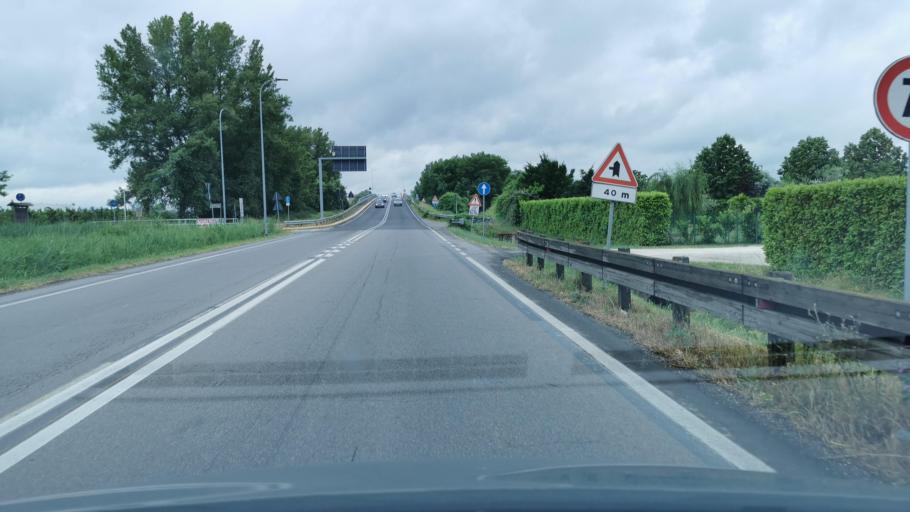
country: IT
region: Emilia-Romagna
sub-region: Provincia di Ravenna
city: Granarolo
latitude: 44.3257
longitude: 11.9082
